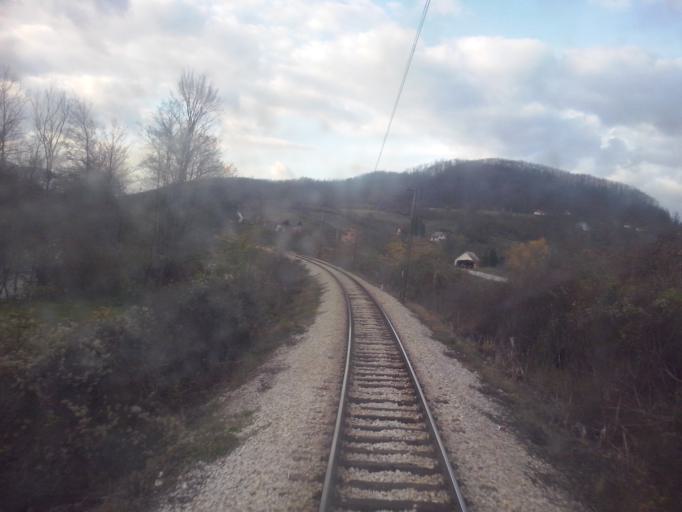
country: RS
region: Central Serbia
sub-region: Zlatiborski Okrug
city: Kosjeric
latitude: 43.9755
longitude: 19.9530
